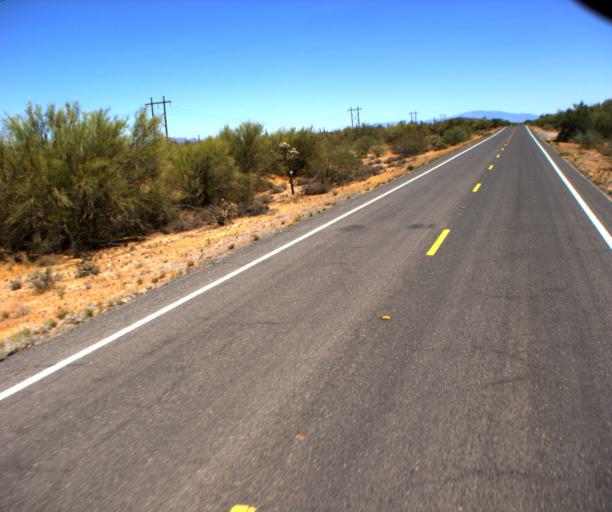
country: US
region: Arizona
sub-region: Pinal County
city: Florence
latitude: 32.8031
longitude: -111.1854
